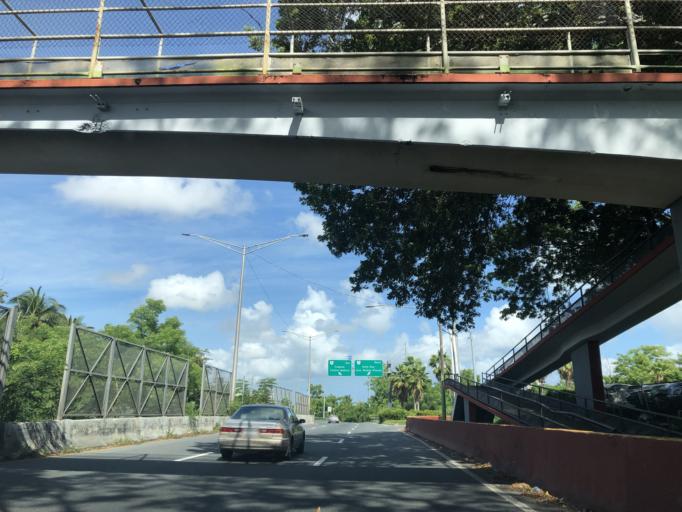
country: PR
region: Trujillo Alto
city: Trujillo Alto
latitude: 18.3963
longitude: -66.0526
